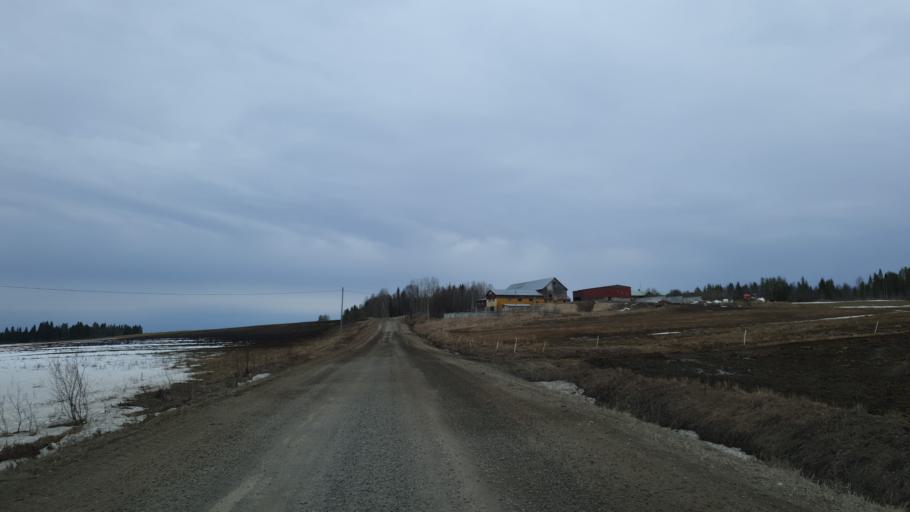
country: SE
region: Vaesterbotten
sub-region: Skelleftea Kommun
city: Burea
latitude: 64.3394
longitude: 21.1273
